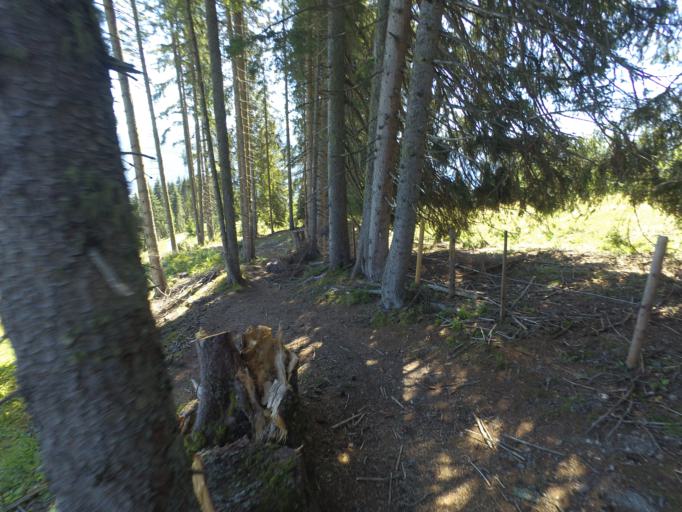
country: AT
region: Salzburg
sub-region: Politischer Bezirk Sankt Johann im Pongau
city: Goldegg
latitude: 47.3375
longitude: 13.0672
